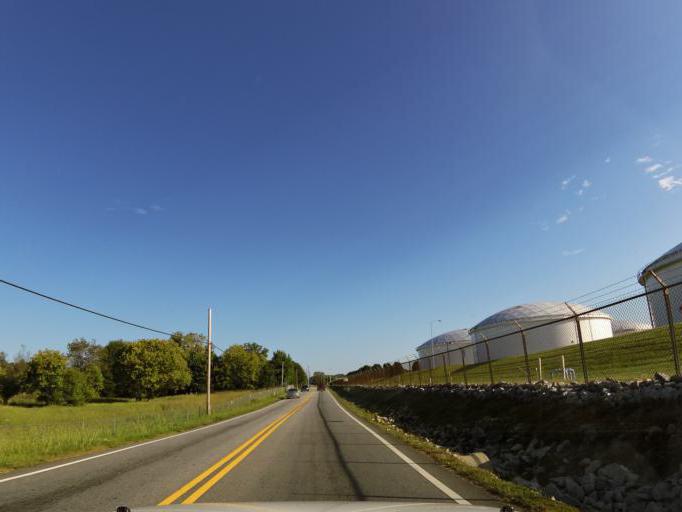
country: US
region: Georgia
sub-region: Cobb County
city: Austell
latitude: 33.8591
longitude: -84.6326
